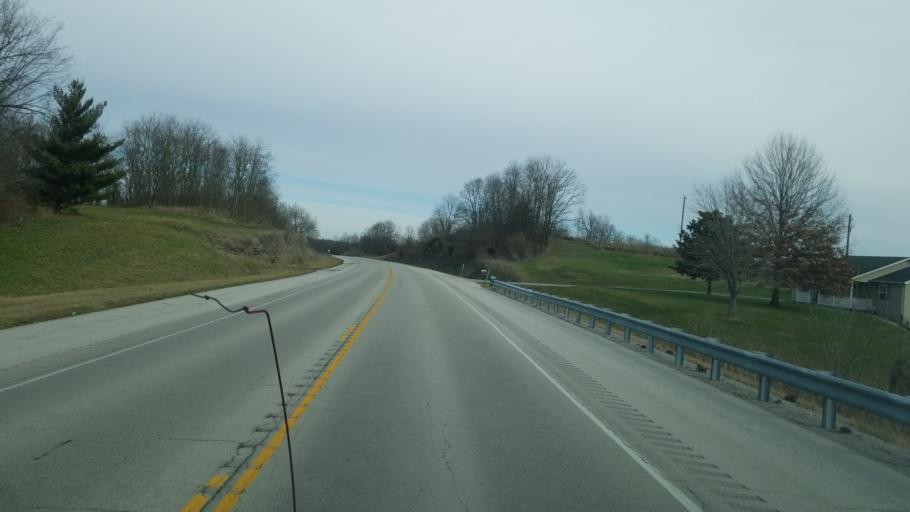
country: US
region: Kentucky
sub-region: Robertson County
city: Mount Olivet
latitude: 38.4637
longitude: -83.9181
